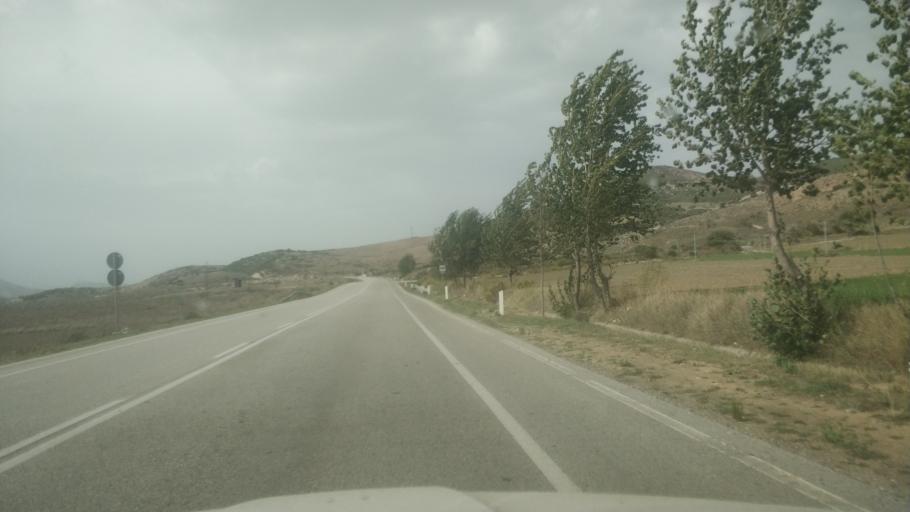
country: AL
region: Gjirokaster
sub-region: Rrethi i Tepelenes
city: Memaliaj
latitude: 40.3604
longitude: 19.9297
